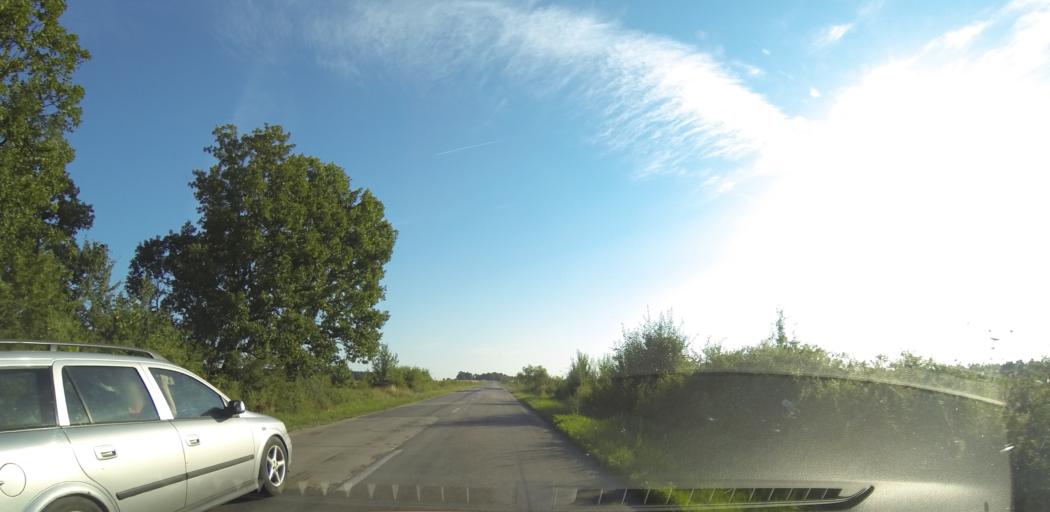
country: RO
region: Valcea
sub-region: Comuna Balcesti
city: Balcesti
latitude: 44.5996
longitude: 23.9279
